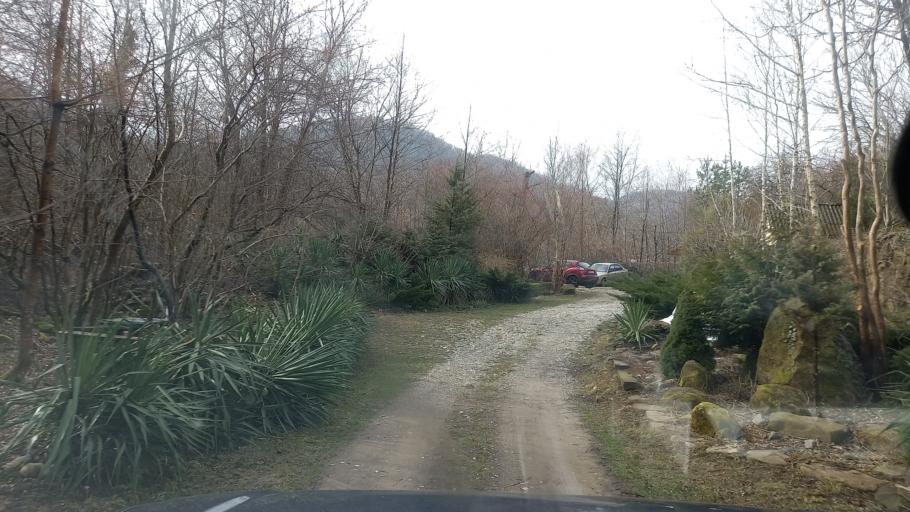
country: RU
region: Krasnodarskiy
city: Dzhubga
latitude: 44.4140
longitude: 38.7203
